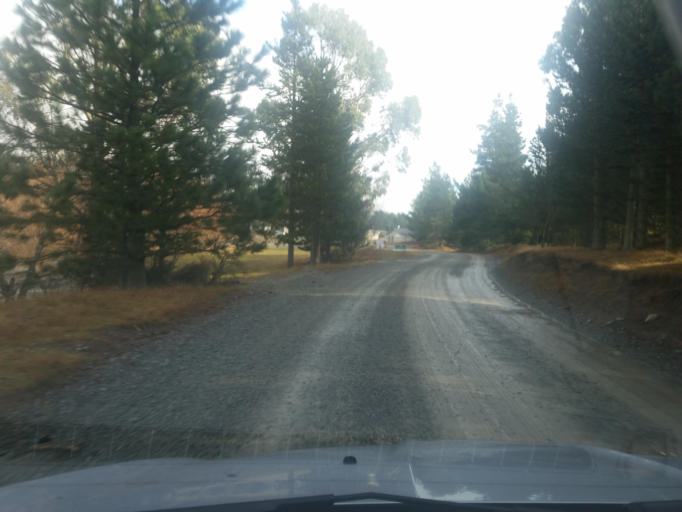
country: NZ
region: Canterbury
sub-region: Ashburton District
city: Methven
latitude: -43.6119
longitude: 171.0513
